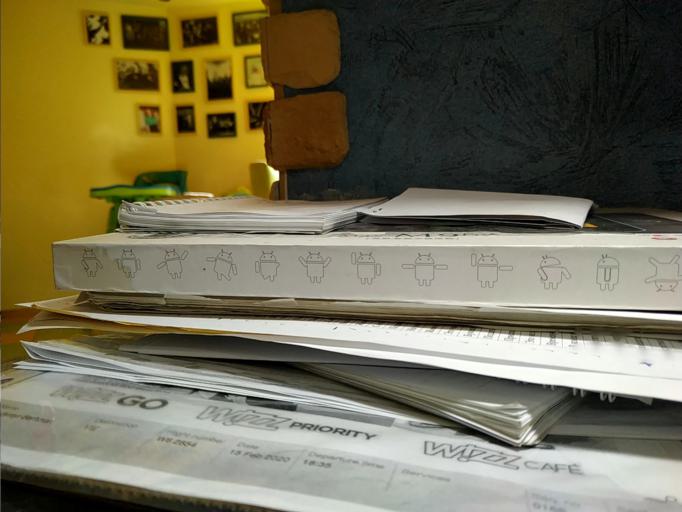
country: RU
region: Novgorod
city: Volot
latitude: 57.7297
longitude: 30.6262
